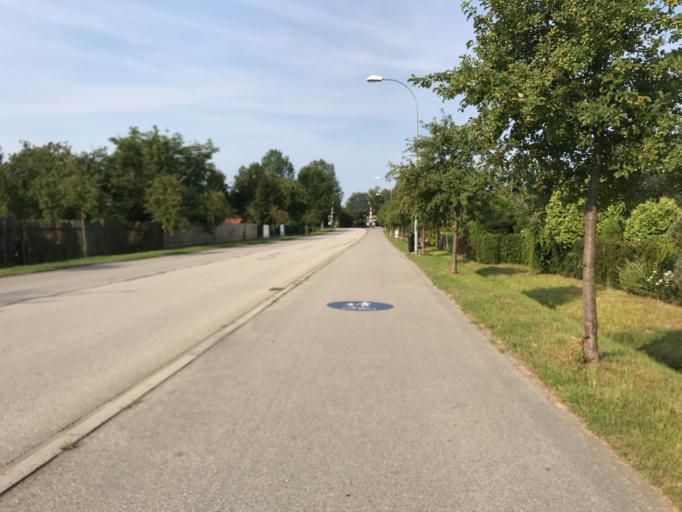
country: CZ
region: Jihocesky
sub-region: Okres Jindrichuv Hradec
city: Trebon
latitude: 49.0081
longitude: 14.7799
